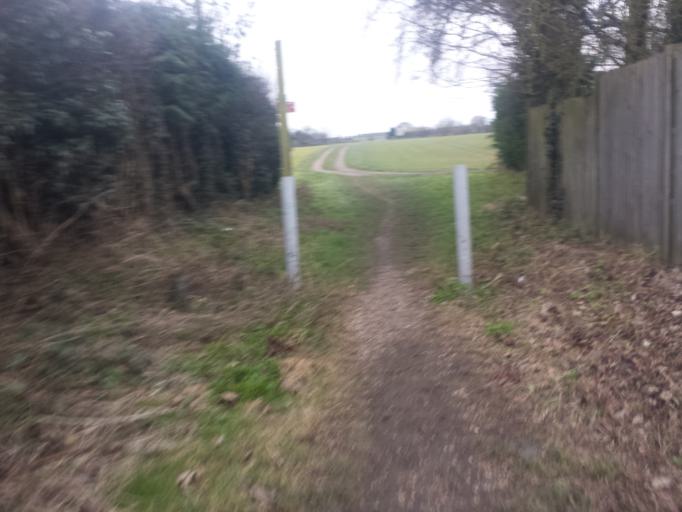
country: GB
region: England
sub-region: Essex
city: Little Clacton
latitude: 51.8552
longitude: 1.1605
